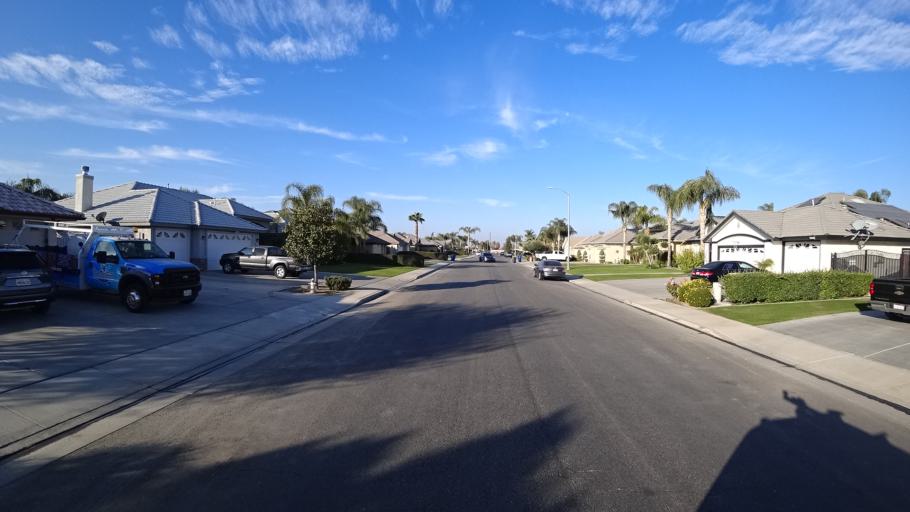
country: US
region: California
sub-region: Kern County
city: Greenfield
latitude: 35.2757
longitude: -119.0538
